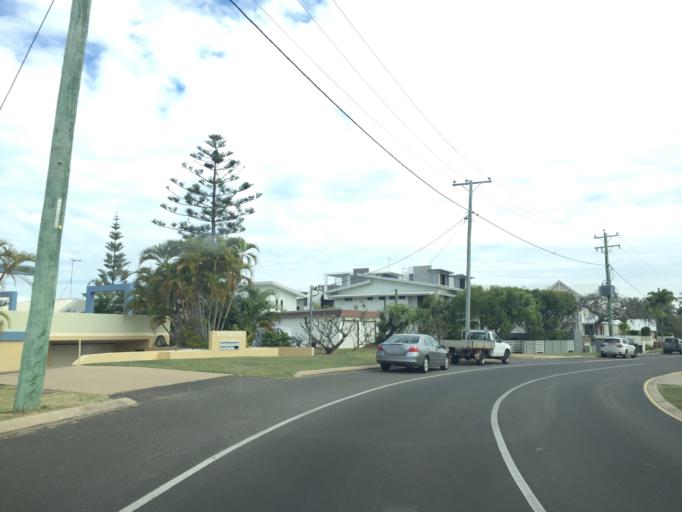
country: AU
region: Queensland
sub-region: Bundaberg
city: Bundaberg
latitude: -24.8182
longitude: 152.4661
